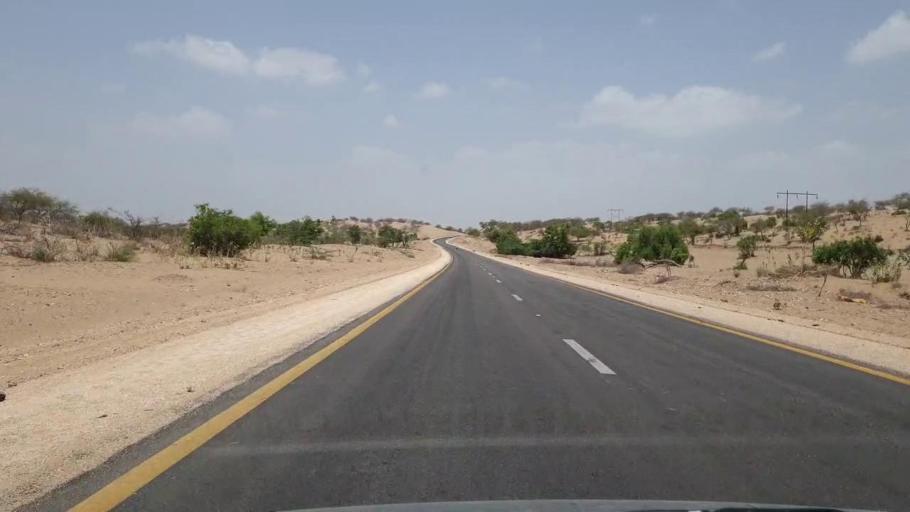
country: PK
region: Sindh
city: Mithi
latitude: 24.8393
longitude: 69.6612
